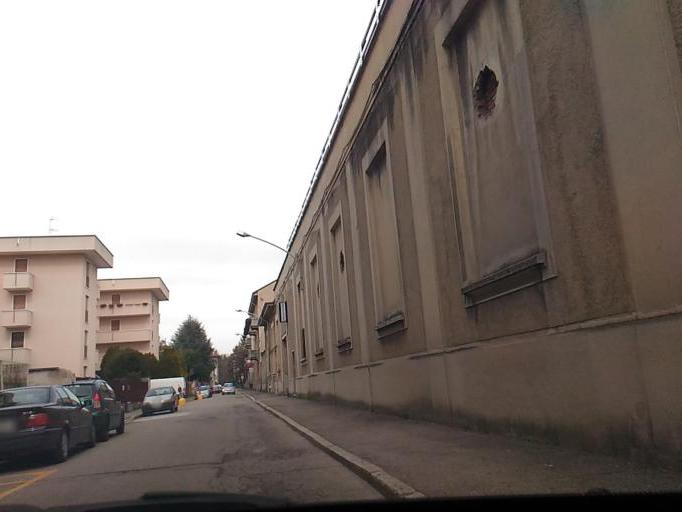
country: IT
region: Lombardy
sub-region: Provincia di Varese
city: Busto Arsizio
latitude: 45.6171
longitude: 8.8458
